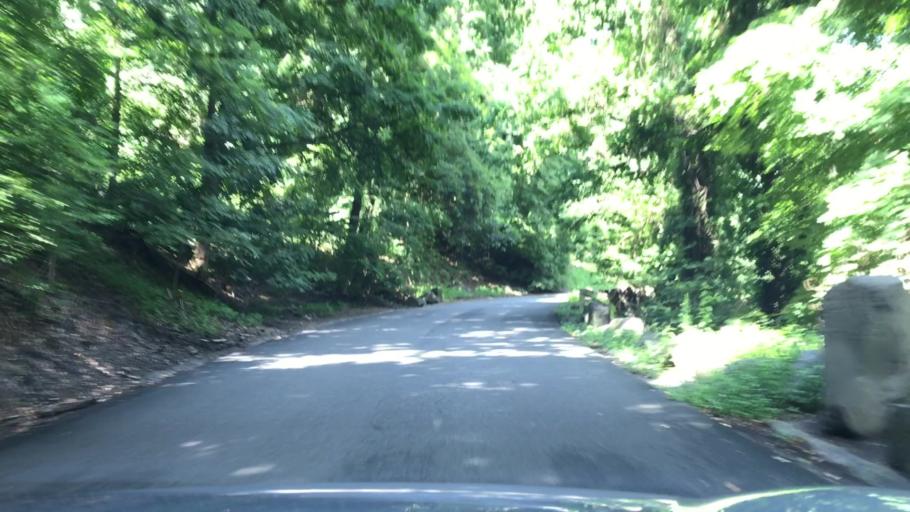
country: US
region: New Jersey
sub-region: Bergen County
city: Englewood Cliffs
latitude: 40.8717
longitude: -73.9499
